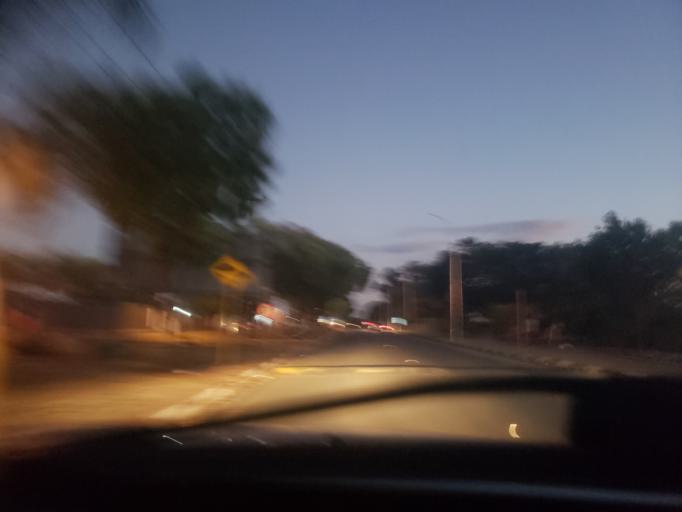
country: BR
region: Sao Paulo
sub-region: Conchal
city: Conchal
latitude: -22.2911
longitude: -47.1334
